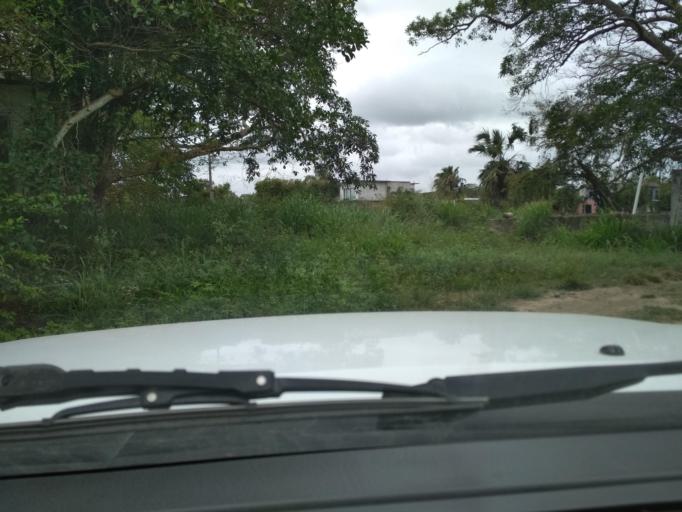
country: MX
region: Veracruz
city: Paso del Toro
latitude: 19.0486
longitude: -96.1372
